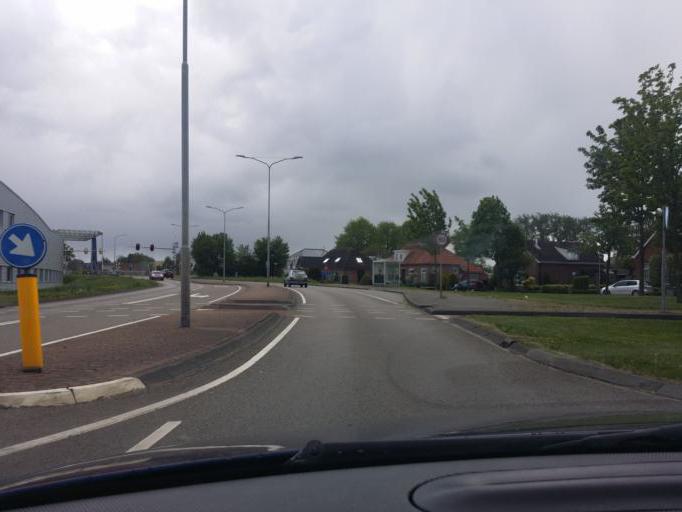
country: NL
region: Groningen
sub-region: Gemeente Hoogezand-Sappemeer
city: Hoogezand
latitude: 53.1728
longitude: 6.7296
